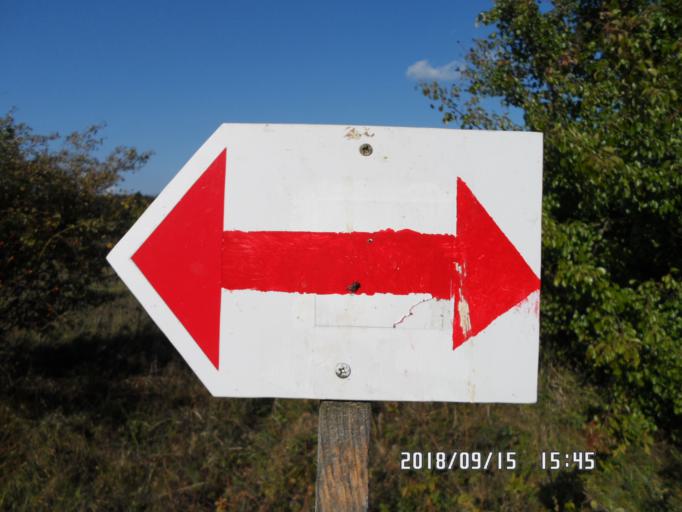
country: HU
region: Fejer
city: Bakonycsernye
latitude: 47.2357
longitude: 18.0521
